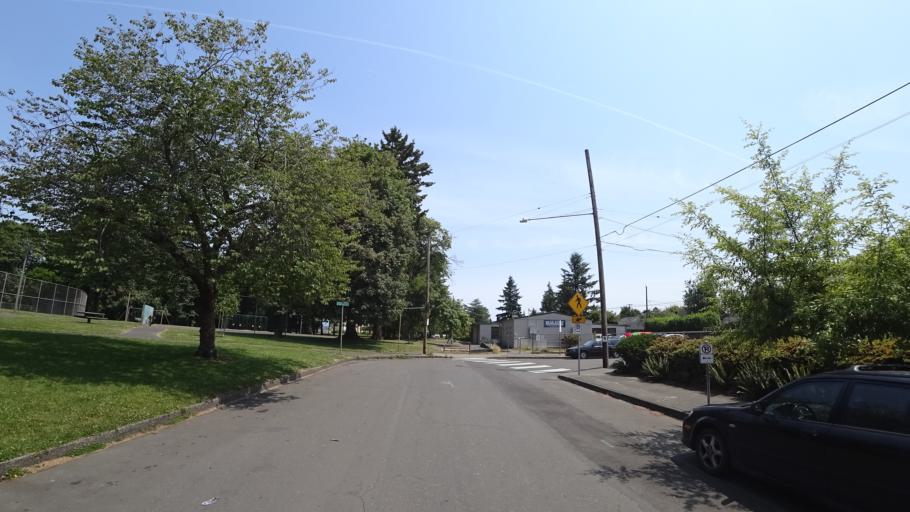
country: US
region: Oregon
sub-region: Multnomah County
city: Portland
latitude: 45.5793
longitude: -122.6711
